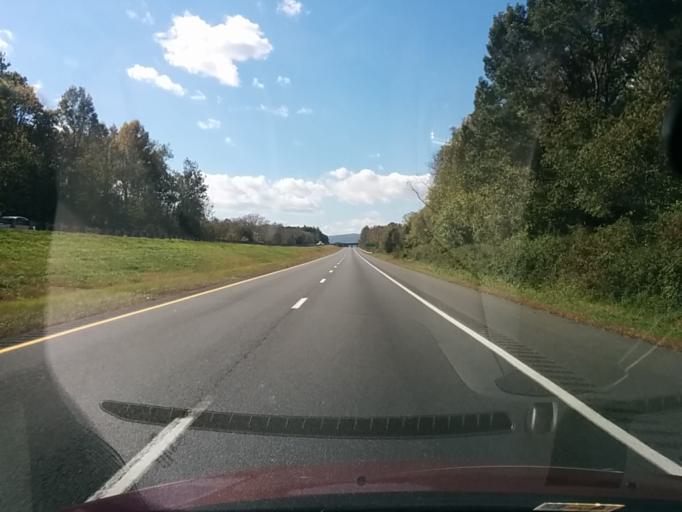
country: US
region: Virginia
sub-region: Albemarle County
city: Crozet
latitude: 38.0469
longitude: -78.7414
